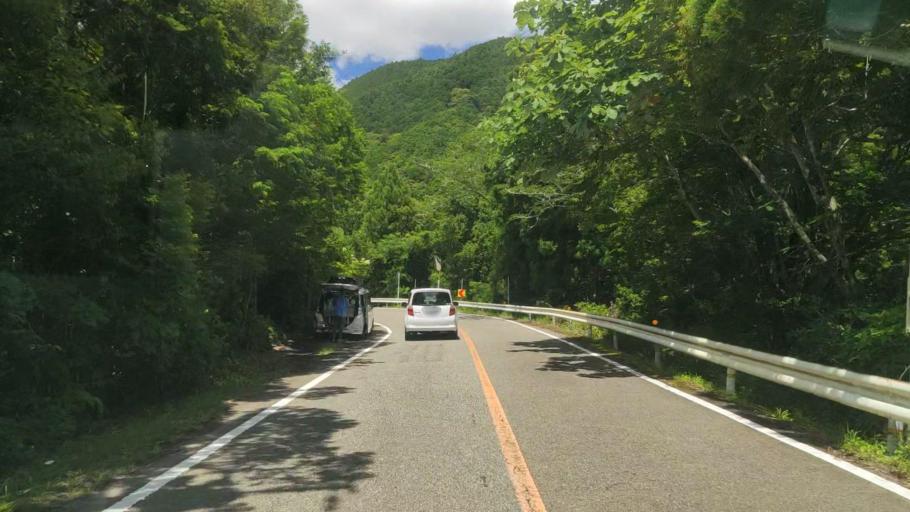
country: JP
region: Mie
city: Owase
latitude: 33.9958
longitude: 136.0257
